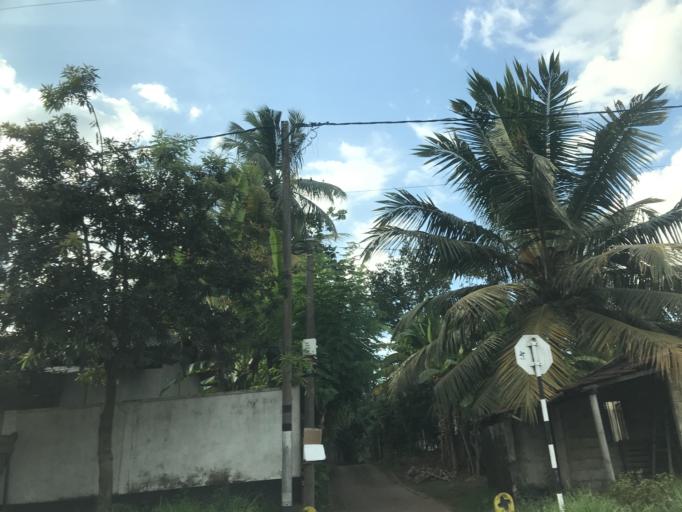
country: LK
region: Western
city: Gampaha
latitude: 7.0524
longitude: 80.0042
